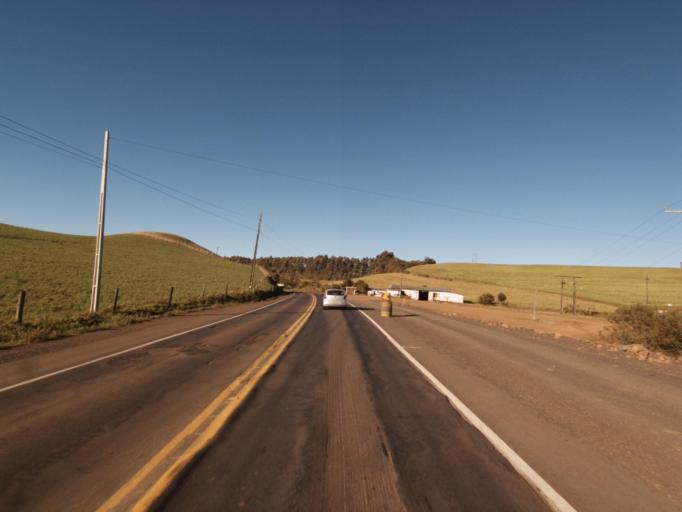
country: AR
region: Misiones
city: Bernardo de Irigoyen
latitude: -26.6158
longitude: -53.5194
